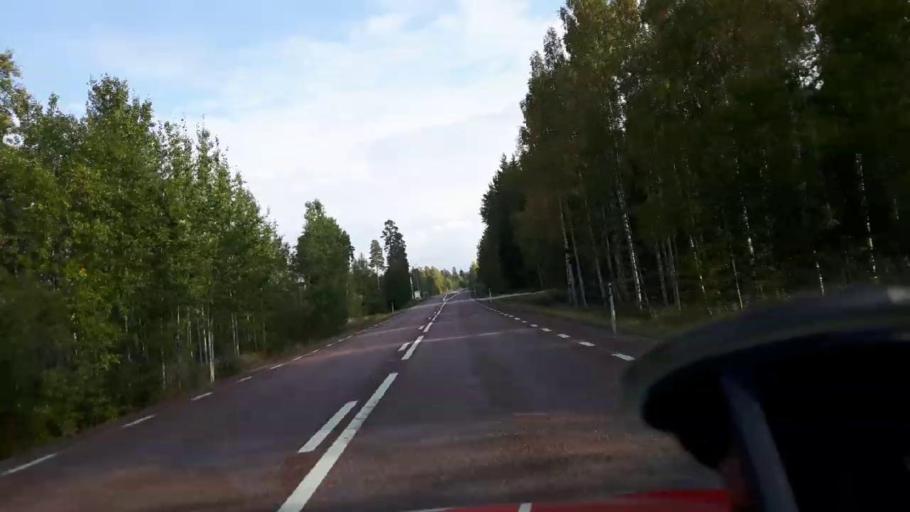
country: SE
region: Gaevleborg
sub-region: Bollnas Kommun
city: Kilafors
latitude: 61.2171
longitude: 16.6733
